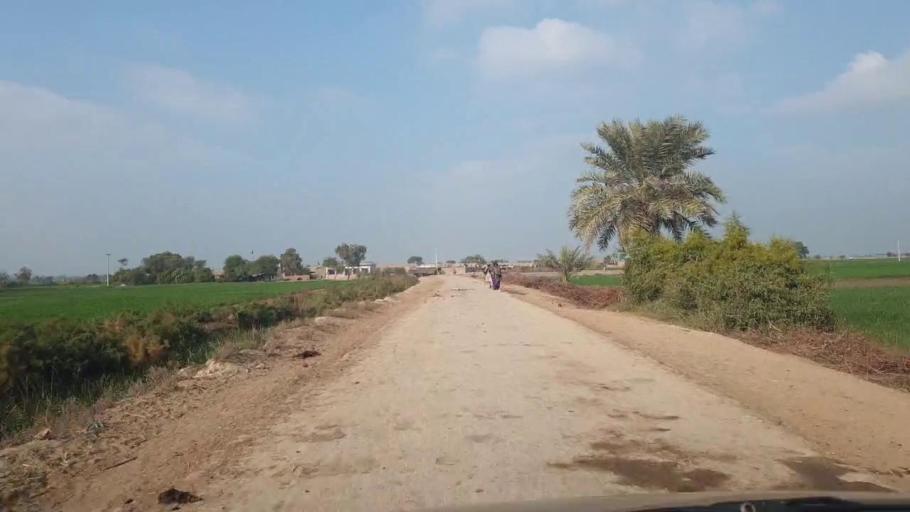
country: PK
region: Sindh
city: Shahdadpur
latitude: 25.9009
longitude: 68.6606
